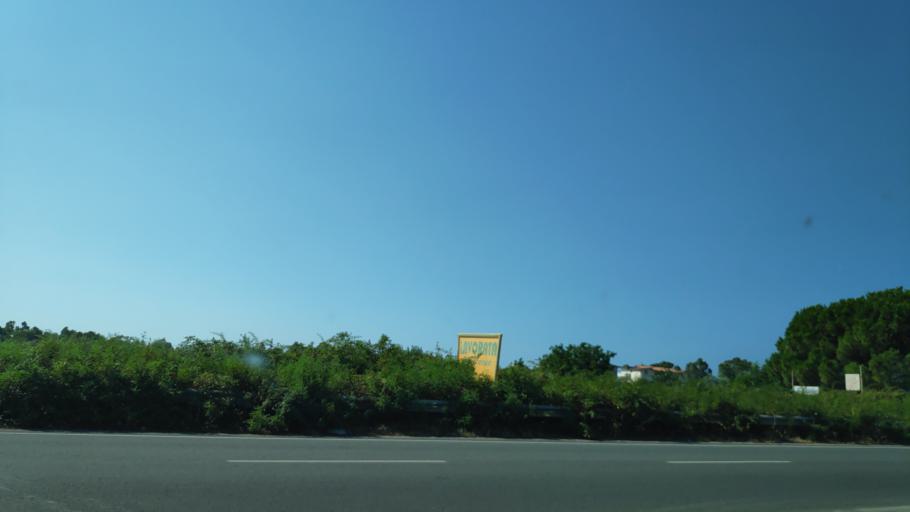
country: IT
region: Calabria
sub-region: Provincia di Reggio Calabria
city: Caulonia Marina
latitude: 38.3372
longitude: 16.4494
